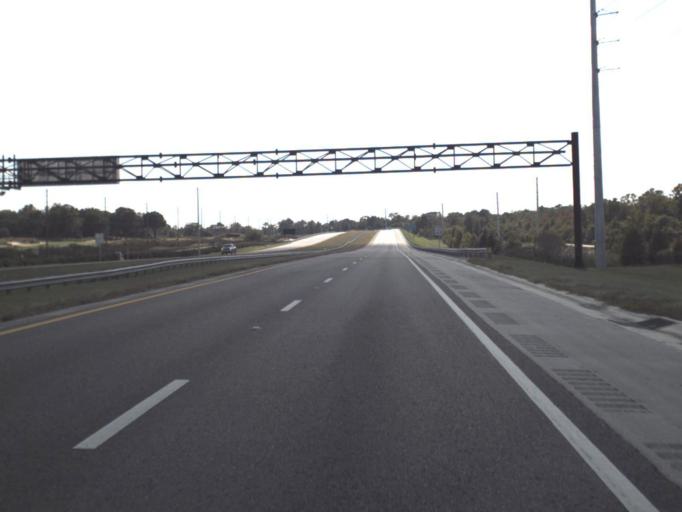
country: US
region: Florida
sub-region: Polk County
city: Citrus Ridge
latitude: 28.3096
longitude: -81.6077
